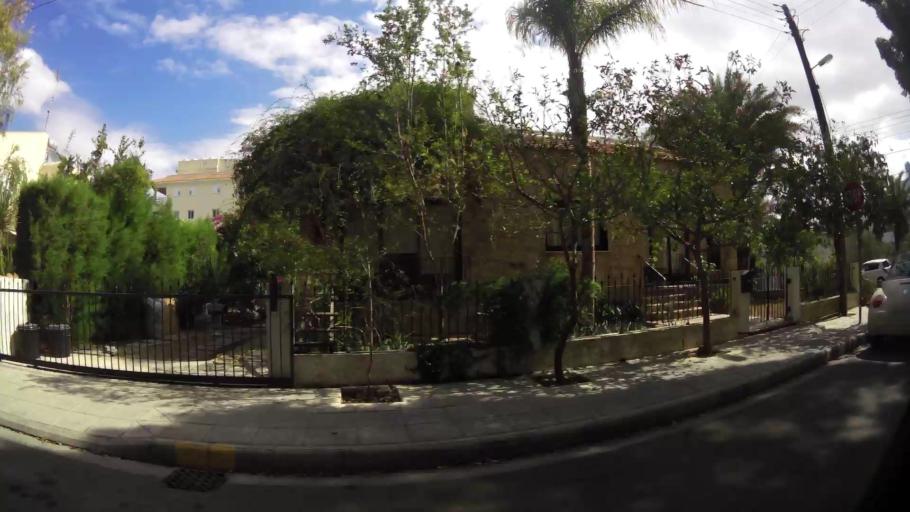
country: CY
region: Lefkosia
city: Nicosia
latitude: 35.1505
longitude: 33.3661
